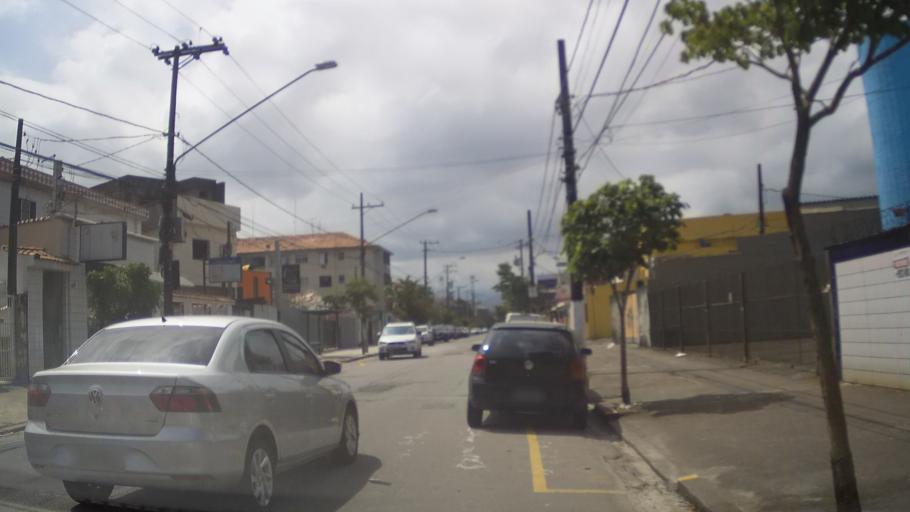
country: BR
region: Sao Paulo
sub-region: Santos
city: Santos
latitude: -23.9652
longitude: -46.3095
